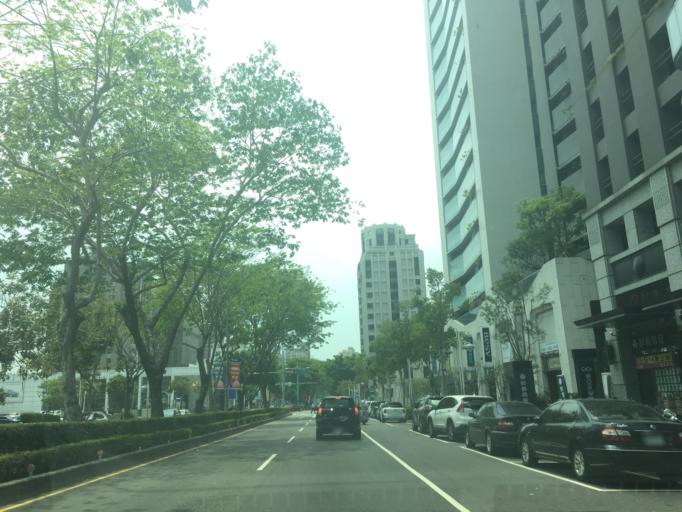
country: TW
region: Taiwan
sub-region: Taichung City
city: Taichung
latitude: 24.1865
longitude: 120.6863
